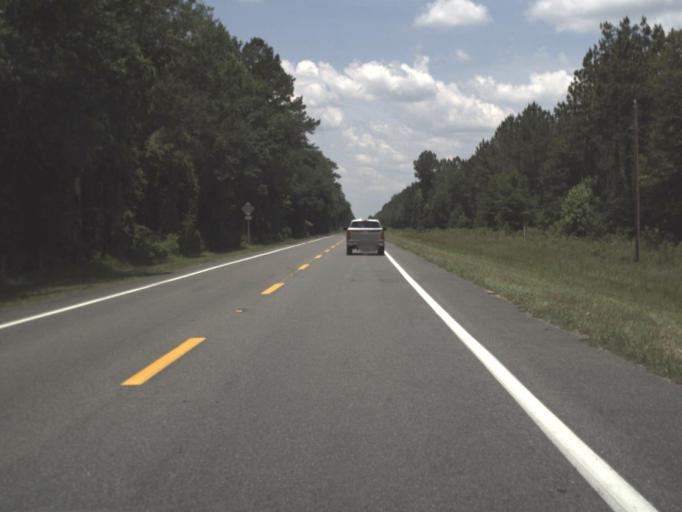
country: US
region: Florida
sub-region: Union County
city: Lake Butler
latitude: 30.0619
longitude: -82.4254
